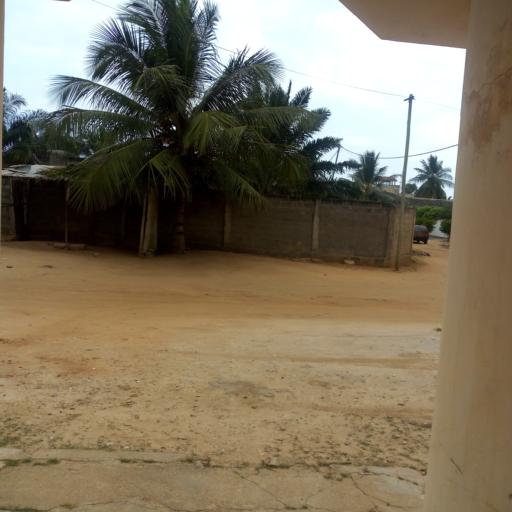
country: TG
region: Maritime
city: Lome
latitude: 6.1714
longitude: 1.1795
